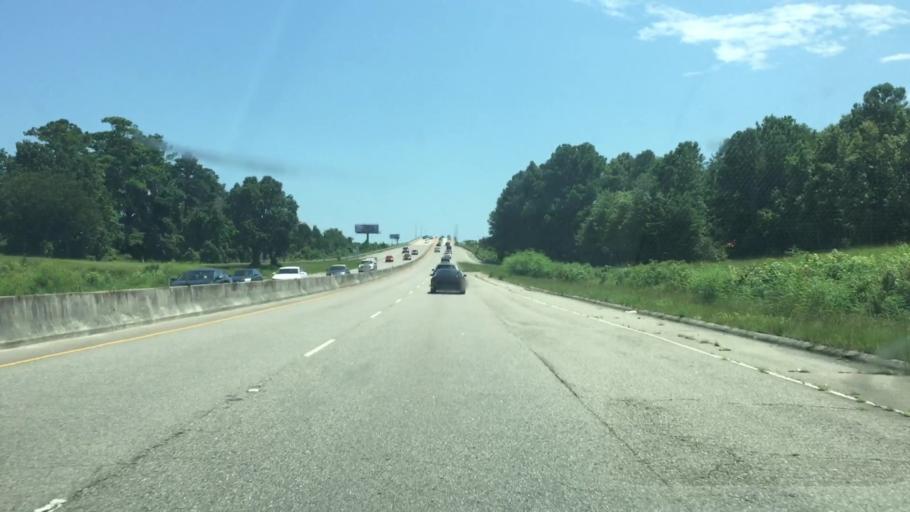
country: US
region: South Carolina
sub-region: Horry County
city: Little River
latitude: 33.8586
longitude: -78.6566
